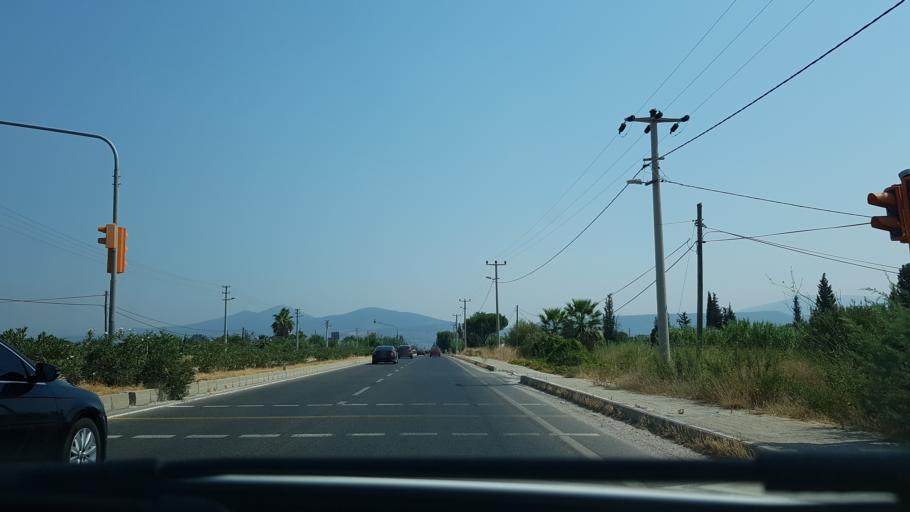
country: TR
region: Mugla
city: Kiulukioi
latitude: 37.2339
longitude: 27.7061
